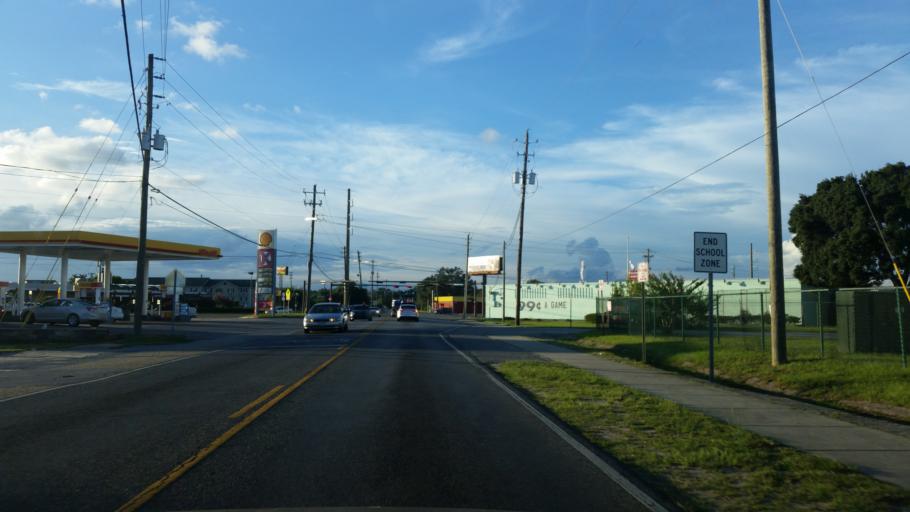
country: US
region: Florida
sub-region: Escambia County
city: Warrington
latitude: 30.4052
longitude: -87.2743
